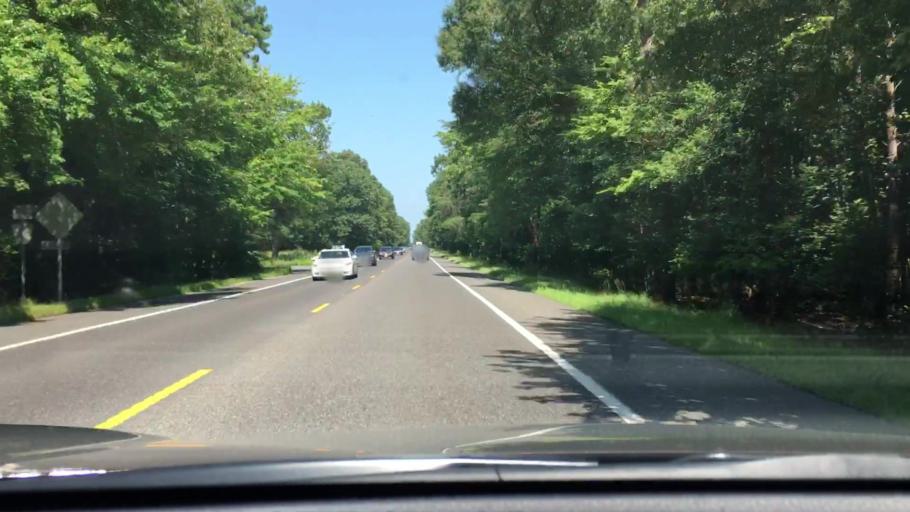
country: US
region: New Jersey
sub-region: Cumberland County
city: Port Norris
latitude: 39.2606
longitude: -74.9320
